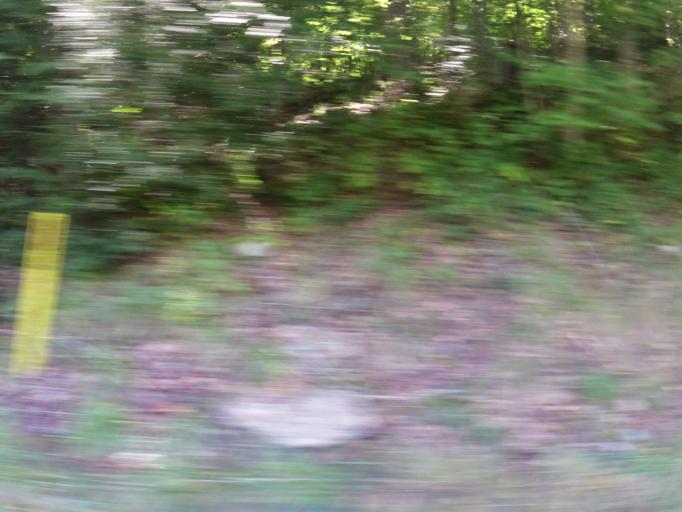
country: US
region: Kentucky
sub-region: Leslie County
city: Hyden
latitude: 37.1530
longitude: -83.4987
